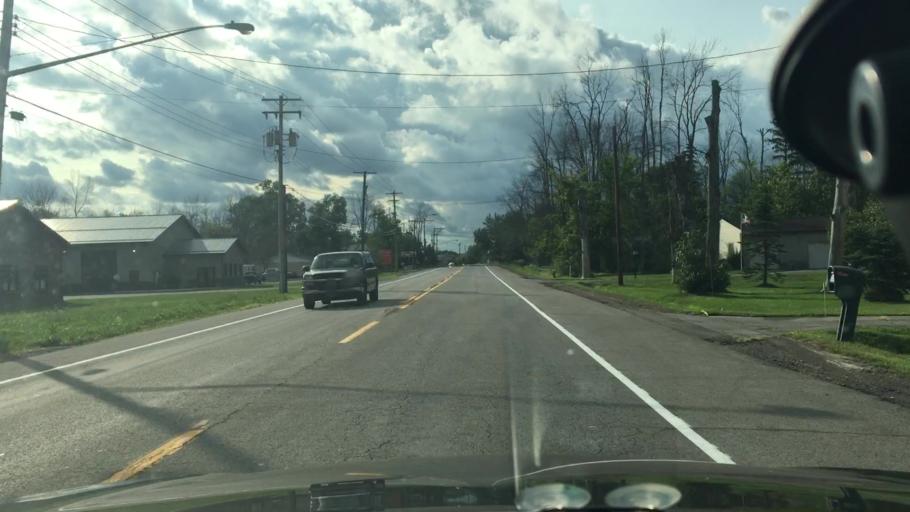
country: US
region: New York
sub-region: Erie County
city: Elma Center
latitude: 42.8241
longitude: -78.6864
